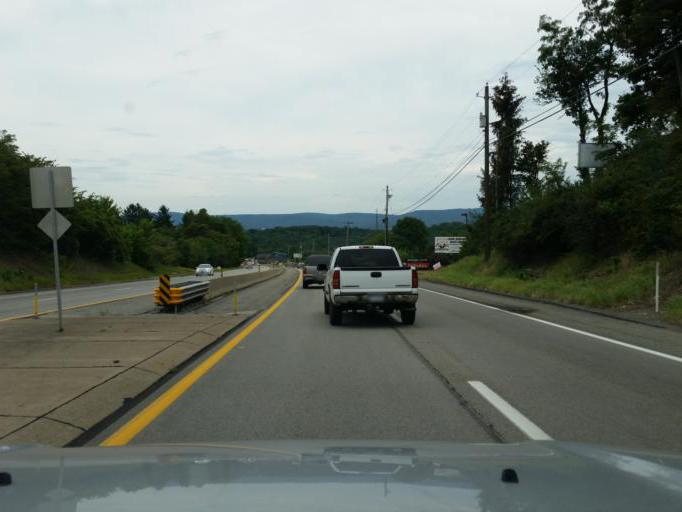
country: US
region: Pennsylvania
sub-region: Westmoreland County
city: Lawson Heights
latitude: 40.2900
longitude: -79.4629
